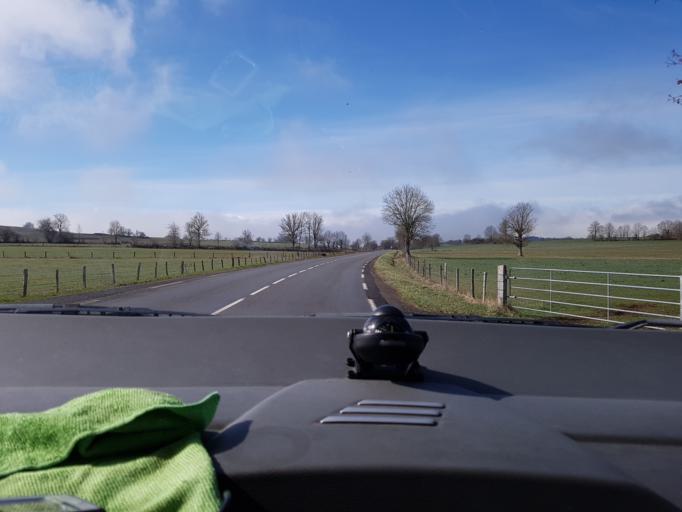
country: FR
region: Auvergne
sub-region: Departement du Cantal
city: Neuveglise
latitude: 44.9459
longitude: 3.0071
